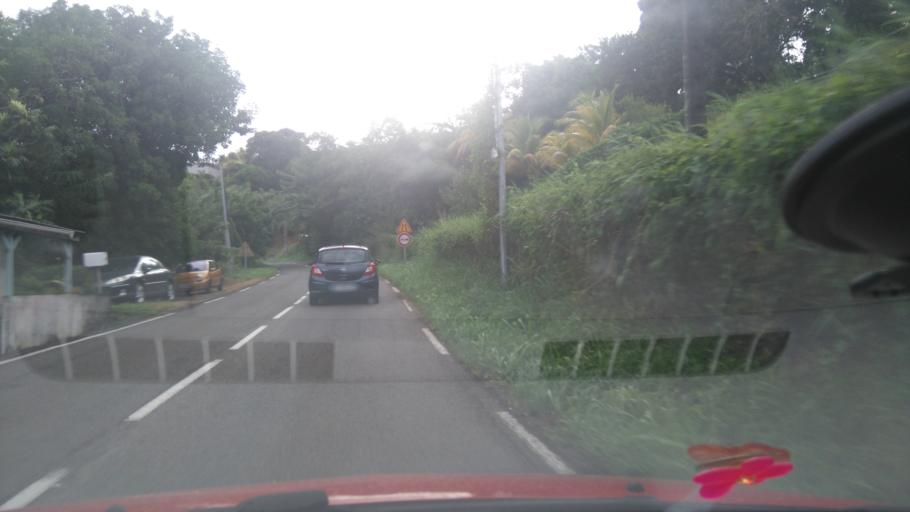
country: MQ
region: Martinique
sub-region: Martinique
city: Saint-Esprit
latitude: 14.5573
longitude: -60.9497
